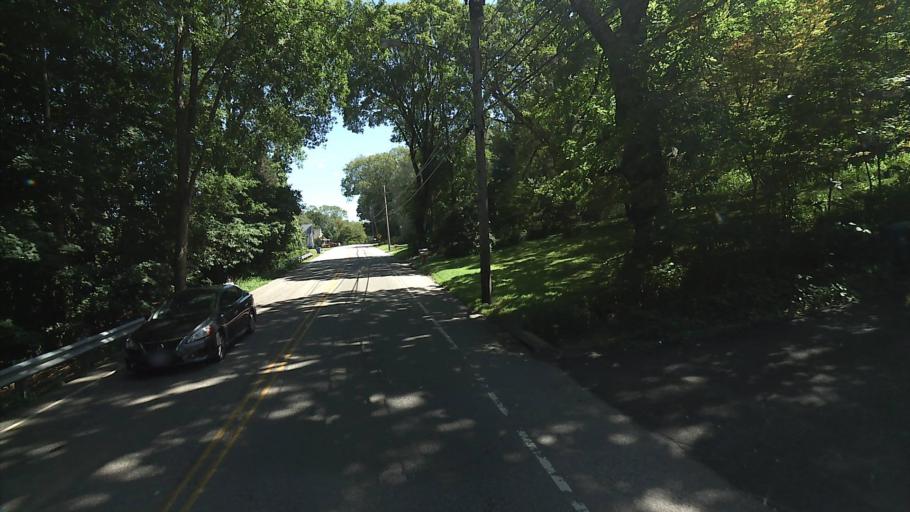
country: US
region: Connecticut
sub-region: New London County
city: Baltic
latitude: 41.5990
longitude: -72.0543
